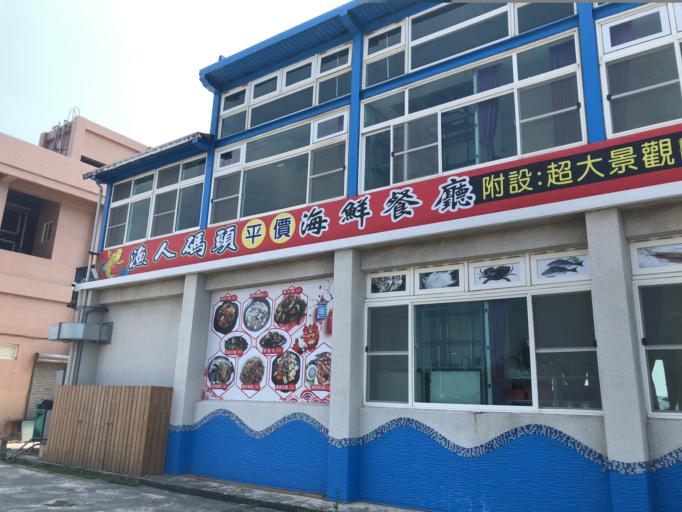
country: TW
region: Taiwan
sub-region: Chiayi
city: Taibao
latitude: 23.4518
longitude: 120.1359
